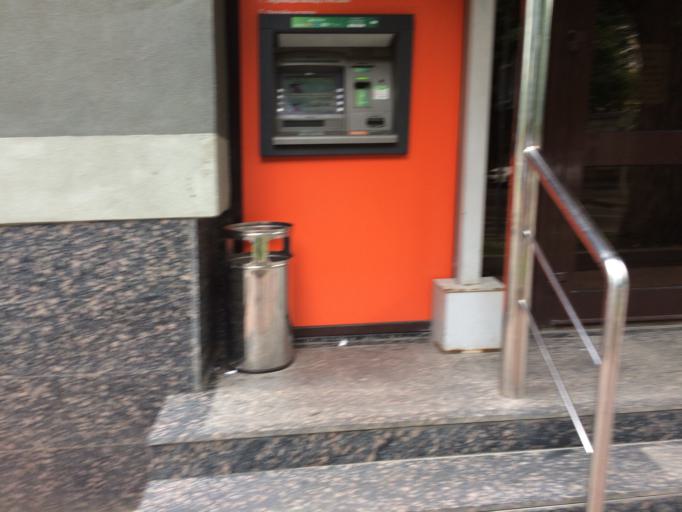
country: RU
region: Stavropol'skiy
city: Stavropol'
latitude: 45.0394
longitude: 41.9666
